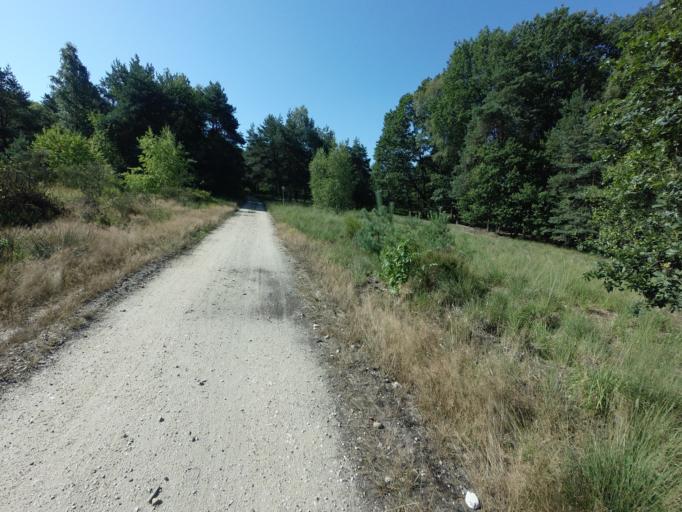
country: DE
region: North Rhine-Westphalia
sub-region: Regierungsbezirk Koln
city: Wassenberg
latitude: 51.1656
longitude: 6.1404
